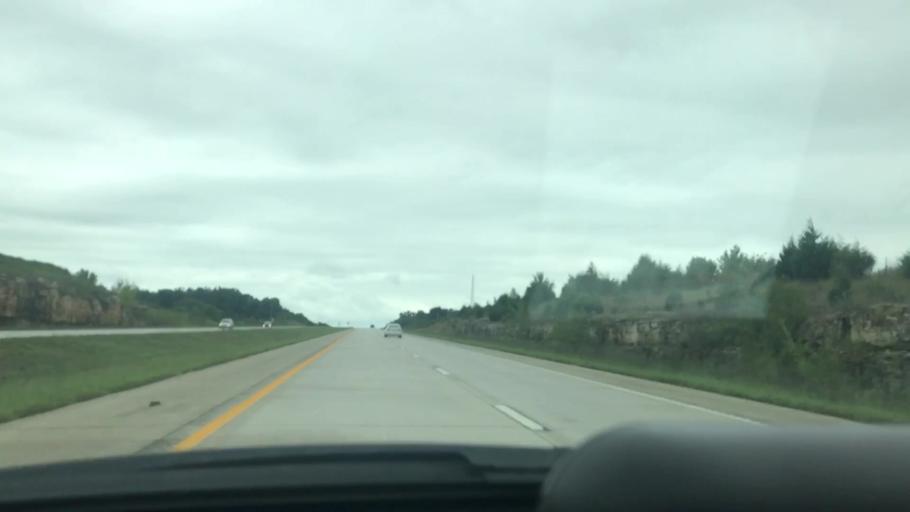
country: US
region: Missouri
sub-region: Dallas County
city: Buffalo
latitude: 37.5354
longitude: -93.1372
